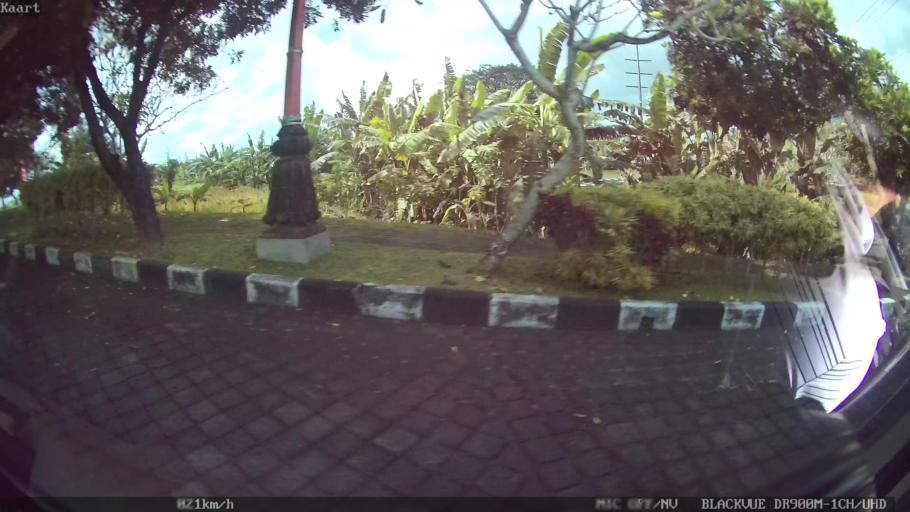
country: ID
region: Bali
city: Banjar Karangsuling
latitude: -8.6013
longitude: 115.1810
